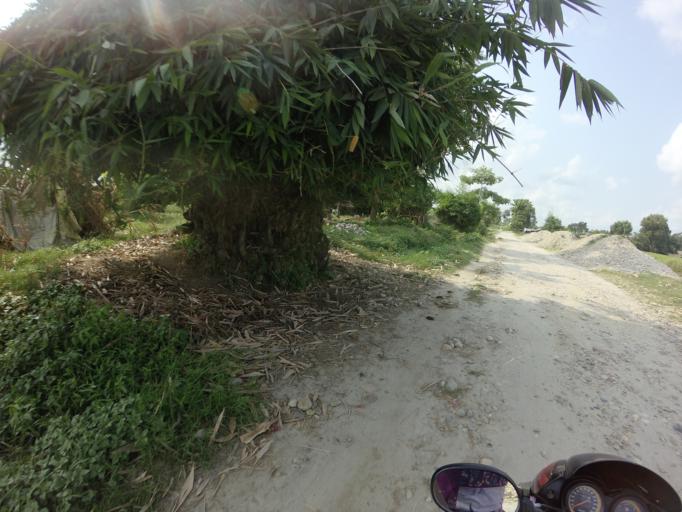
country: NP
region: Far Western
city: Tikapur
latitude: 28.4518
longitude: 81.0727
